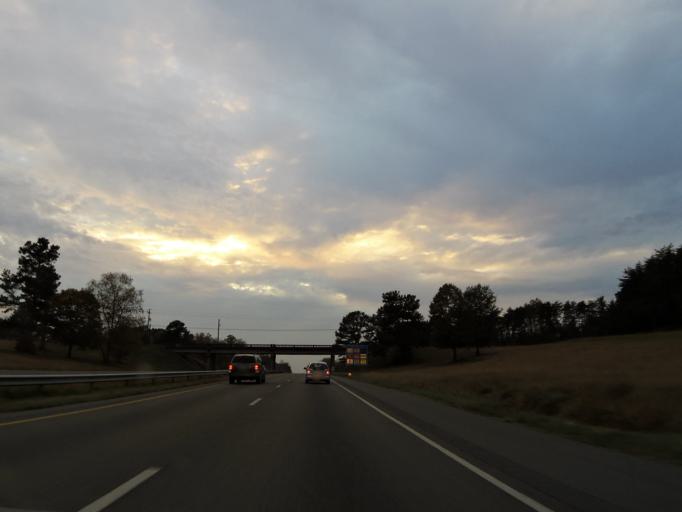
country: US
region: North Carolina
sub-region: Burke County
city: Drexel
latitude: 35.7257
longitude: -81.6349
